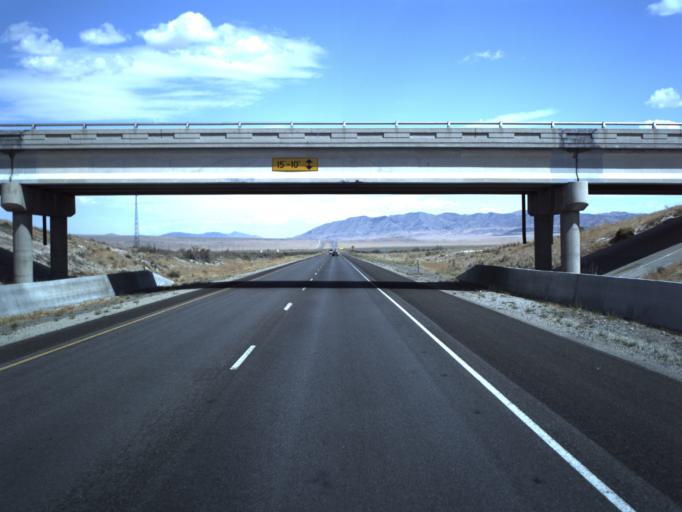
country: US
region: Utah
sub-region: Tooele County
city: Grantsville
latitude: 40.7312
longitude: -113.1146
